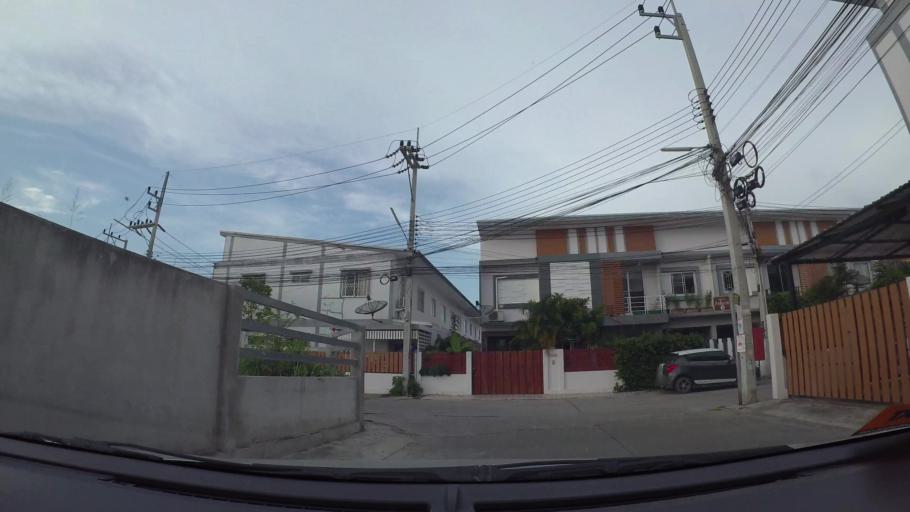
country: TH
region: Chon Buri
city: Chon Buri
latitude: 13.3378
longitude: 100.9834
